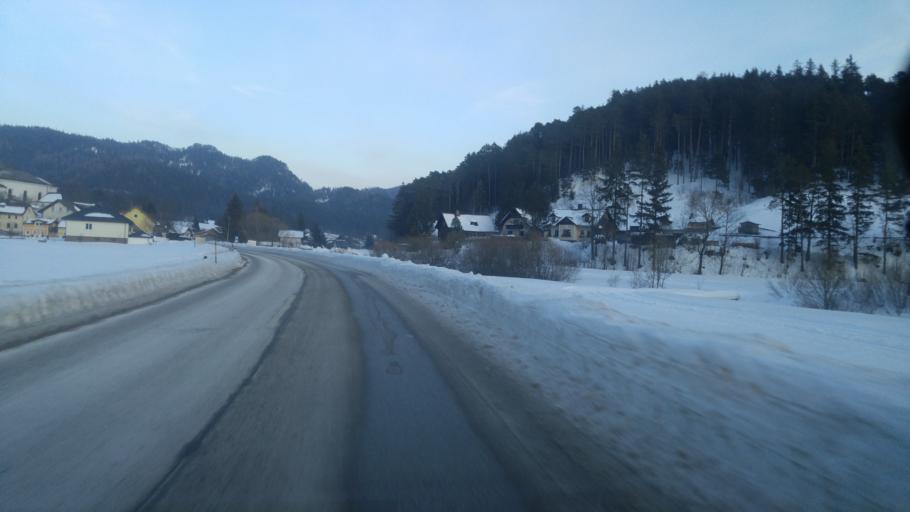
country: AT
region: Lower Austria
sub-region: Politischer Bezirk Wiener Neustadt
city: Rohr im Gebirge
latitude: 47.8942
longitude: 15.7309
